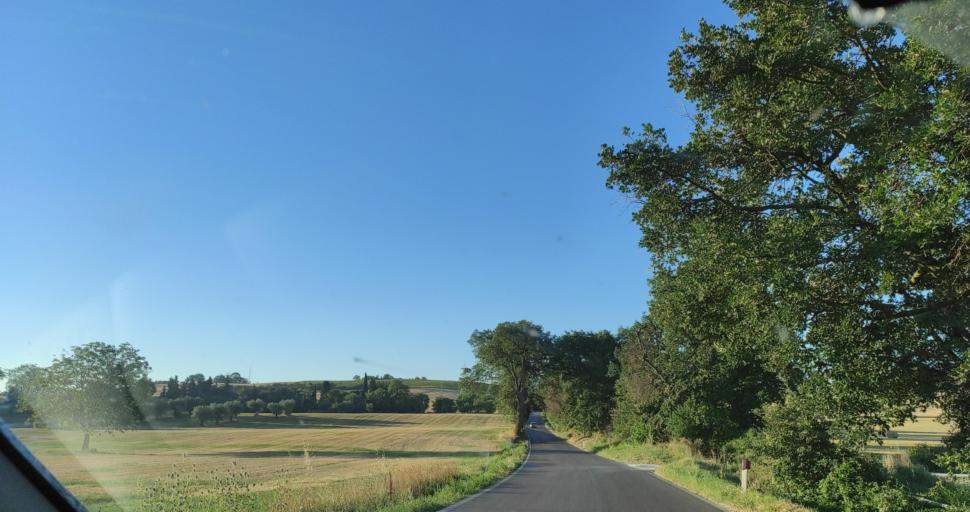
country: IT
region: The Marches
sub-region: Provincia di Macerata
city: Casette Verdini
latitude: 43.2354
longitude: 13.3894
